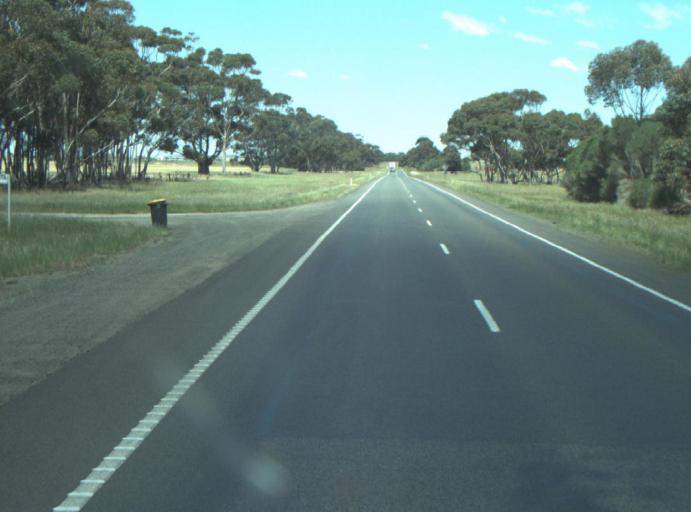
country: AU
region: Victoria
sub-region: Greater Geelong
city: Lara
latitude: -37.9405
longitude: 144.3576
